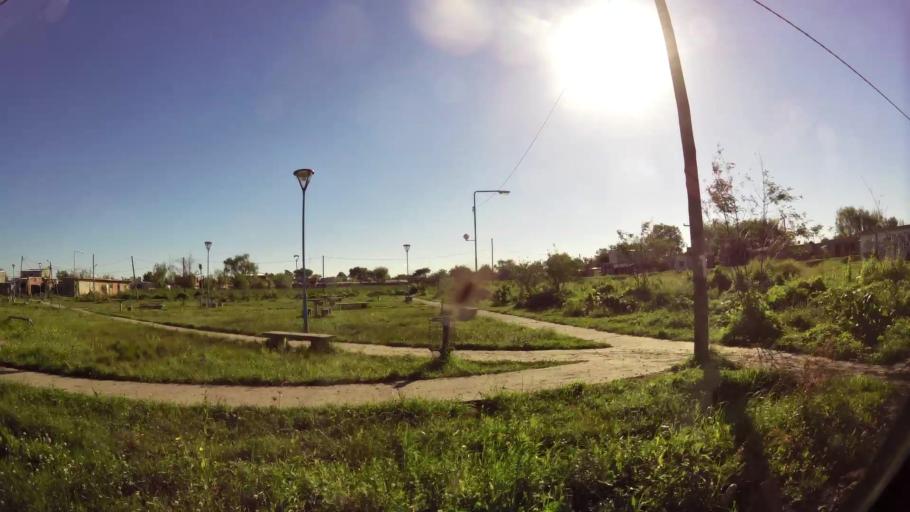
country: AR
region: Buenos Aires
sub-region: Partido de Quilmes
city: Quilmes
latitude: -34.7551
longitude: -58.3198
